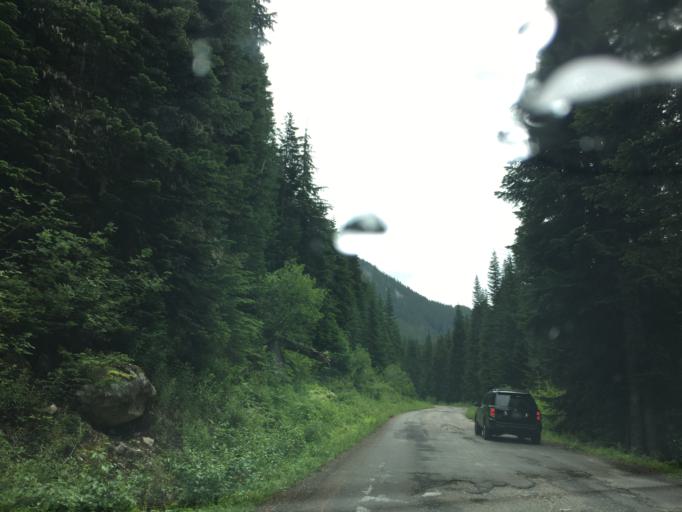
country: US
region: Washington
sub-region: Chelan County
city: Leavenworth
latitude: 47.7484
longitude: -121.0948
